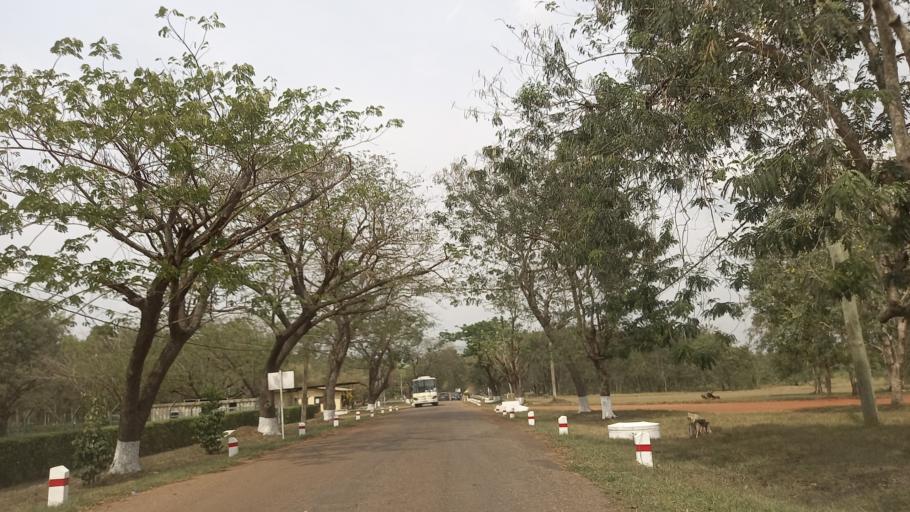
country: GH
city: Akropong
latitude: 6.0944
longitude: 0.1145
